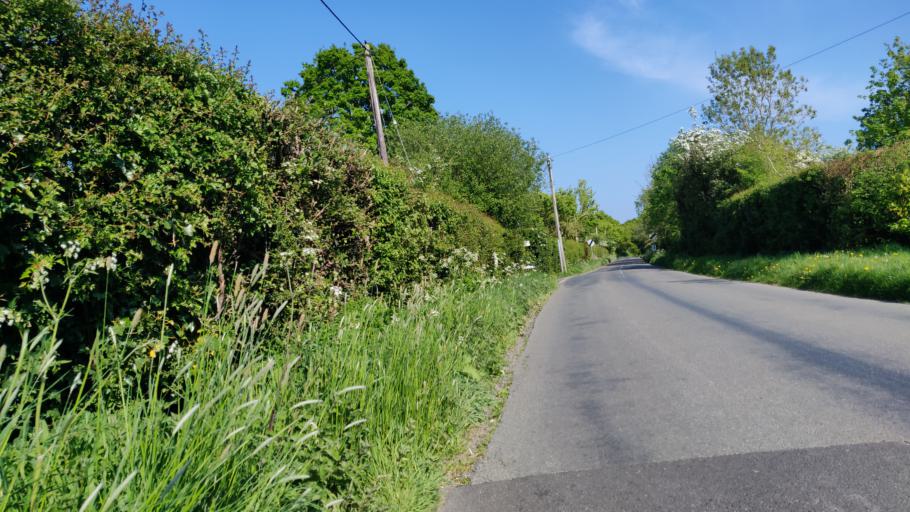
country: GB
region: England
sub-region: West Sussex
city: Southwater
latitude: 51.0294
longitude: -0.3843
